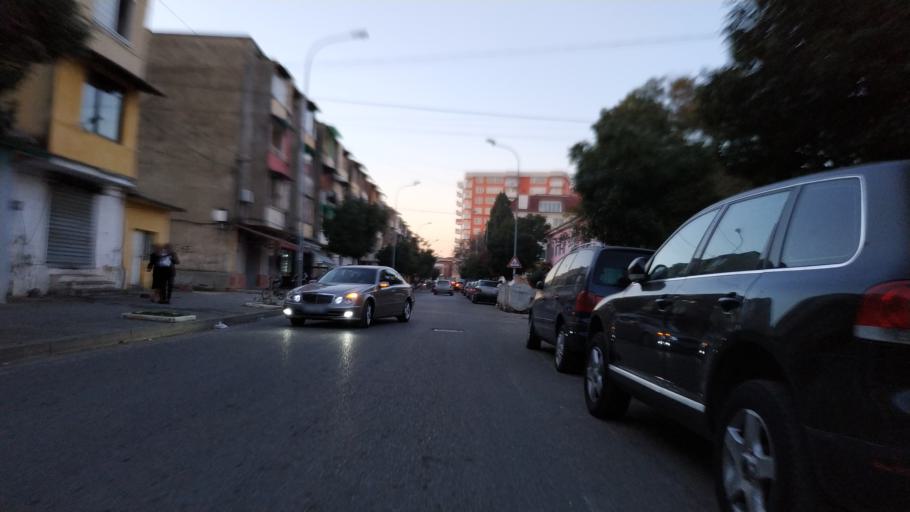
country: AL
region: Shkoder
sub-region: Rrethi i Shkodres
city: Shkoder
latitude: 42.0742
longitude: 19.5194
